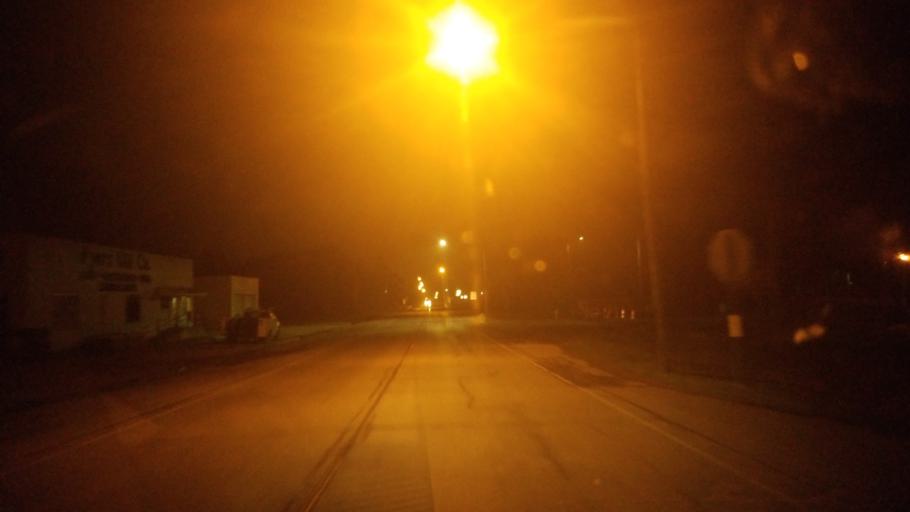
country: US
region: Missouri
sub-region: Pike County
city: Bowling Green
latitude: 39.3451
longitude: -91.2036
